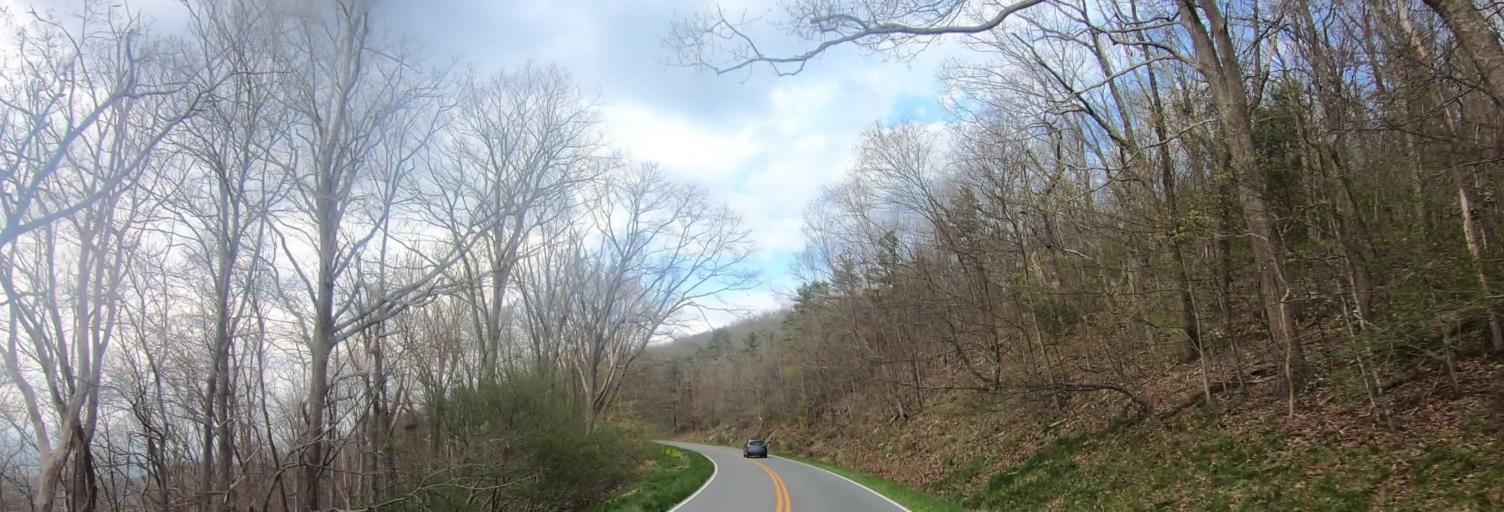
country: US
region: Virginia
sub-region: Augusta County
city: Crimora
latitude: 38.1357
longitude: -78.7815
